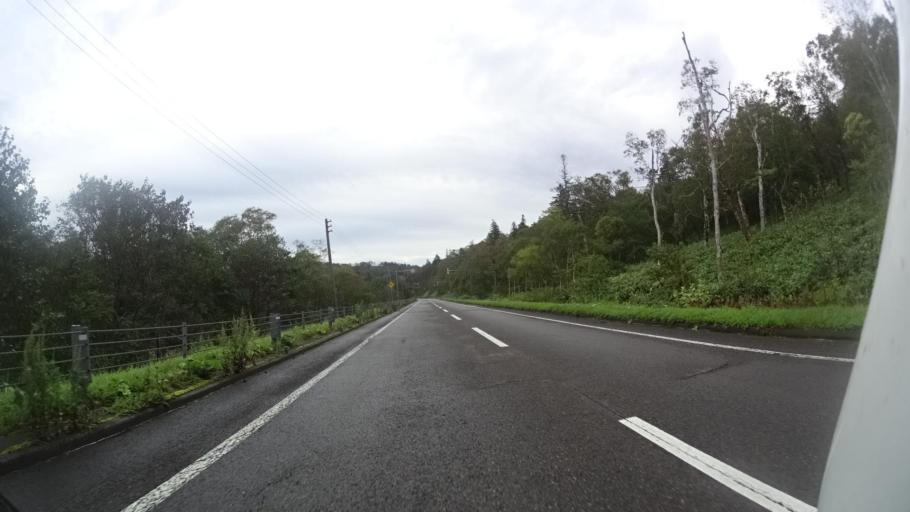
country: JP
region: Hokkaido
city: Shibetsu
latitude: 43.7569
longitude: 144.8093
